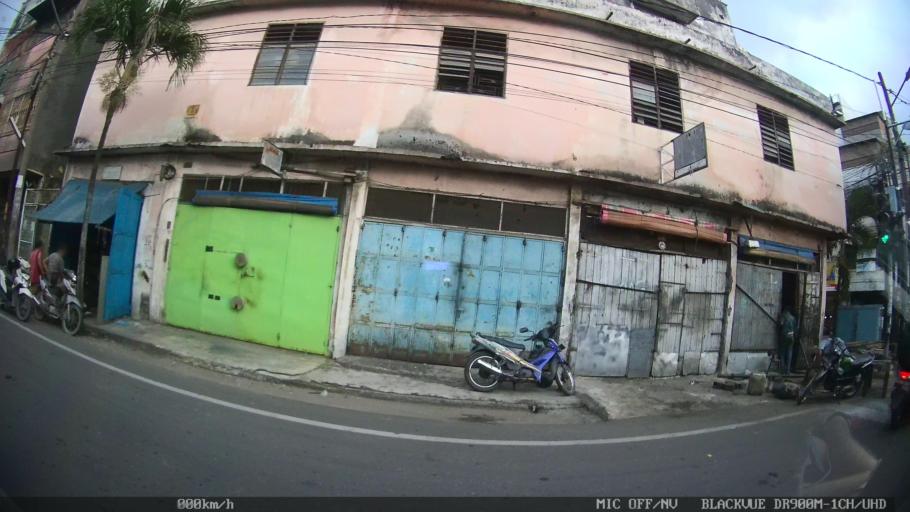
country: ID
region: North Sumatra
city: Medan
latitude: 3.5803
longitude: 98.6890
